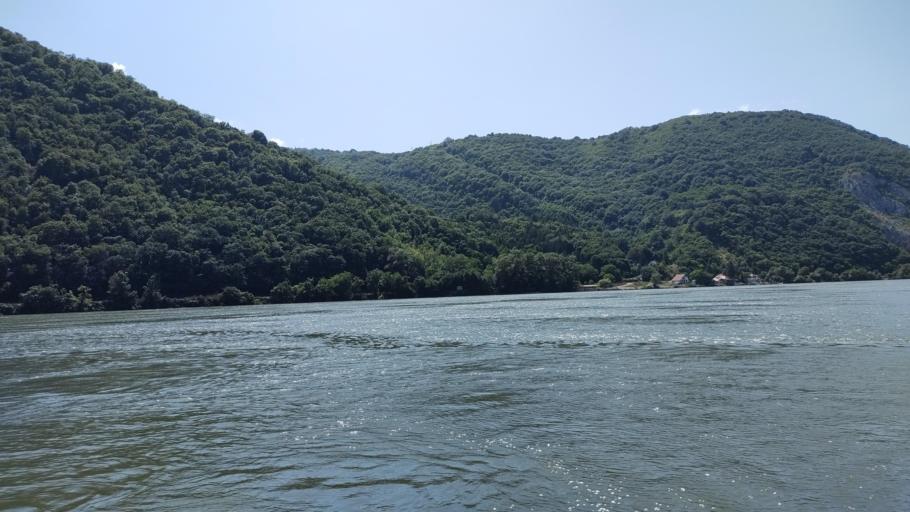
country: RO
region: Caras-Severin
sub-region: Comuna Pescari
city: Coronini
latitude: 44.6555
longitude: 21.7154
